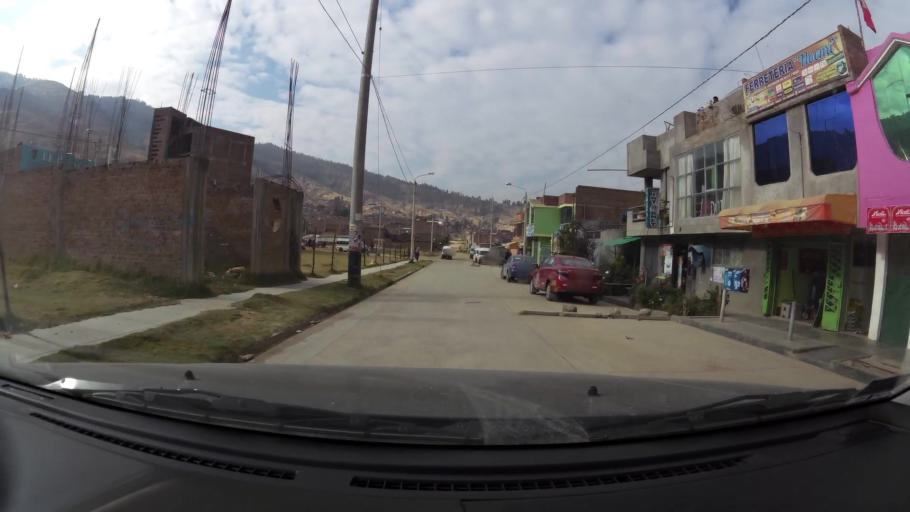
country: PE
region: Junin
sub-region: Provincia de Huancayo
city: Huancayo
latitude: -12.0507
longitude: -75.1884
